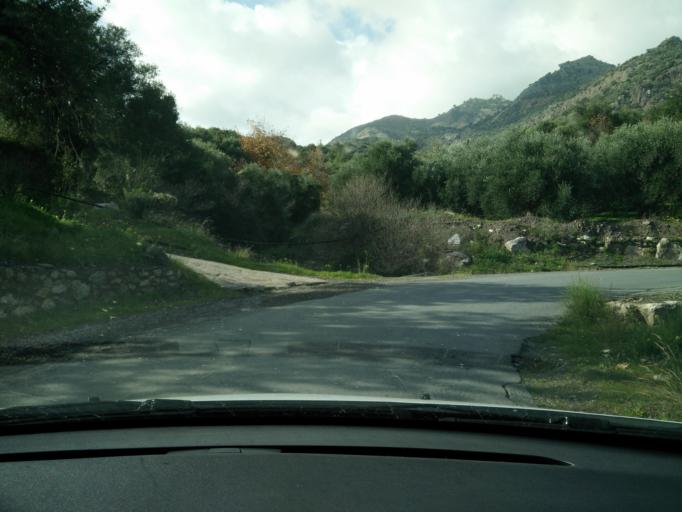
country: GR
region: Crete
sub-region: Nomos Lasithiou
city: Gra Liyia
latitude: 35.0331
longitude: 25.5752
